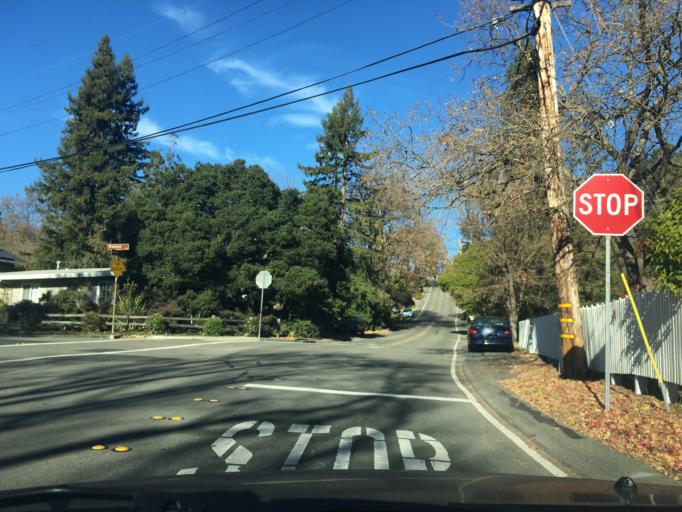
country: US
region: California
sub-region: Contra Costa County
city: Lafayette
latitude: 37.8730
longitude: -122.1006
